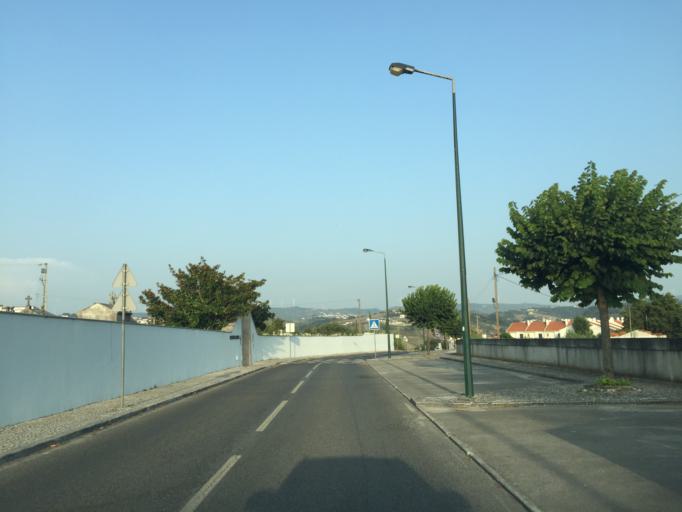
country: PT
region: Leiria
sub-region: Batalha
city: Batalha
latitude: 39.6607
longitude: -8.8319
